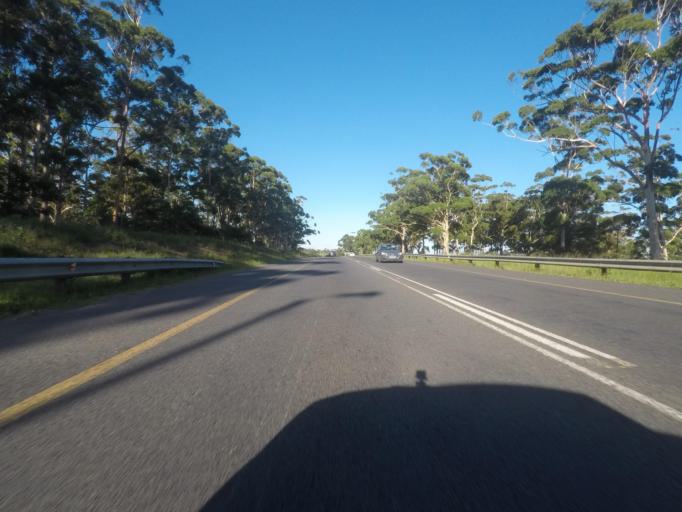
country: ZA
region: Eastern Cape
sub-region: Buffalo City Metropolitan Municipality
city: East London
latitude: -33.0460
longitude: 27.8244
